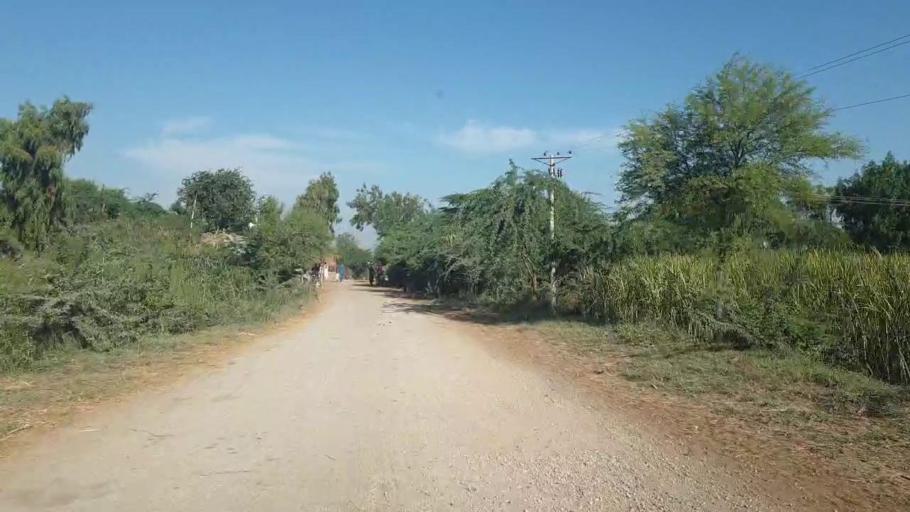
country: PK
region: Sindh
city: Talhar
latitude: 24.9091
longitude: 68.8086
